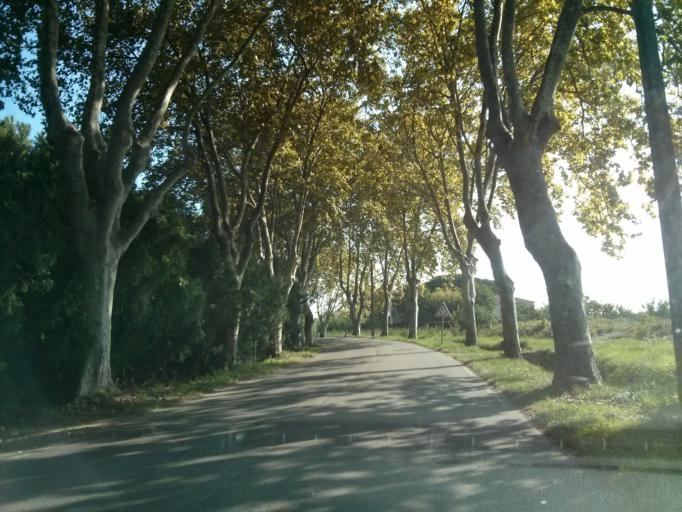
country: FR
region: Languedoc-Roussillon
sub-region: Departement du Gard
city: Aigues-Vives
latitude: 43.7293
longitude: 4.1888
